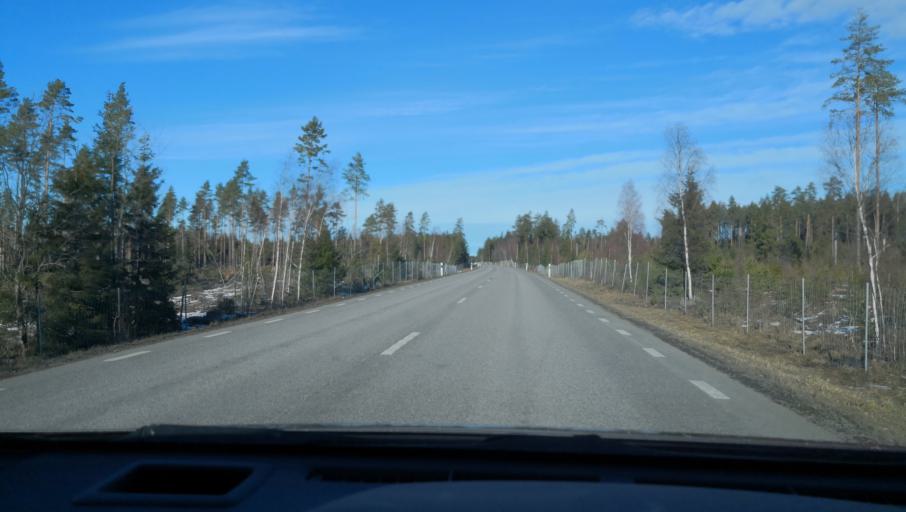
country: SE
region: Uppsala
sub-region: Uppsala Kommun
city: Vattholma
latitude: 60.0412
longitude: 17.7510
